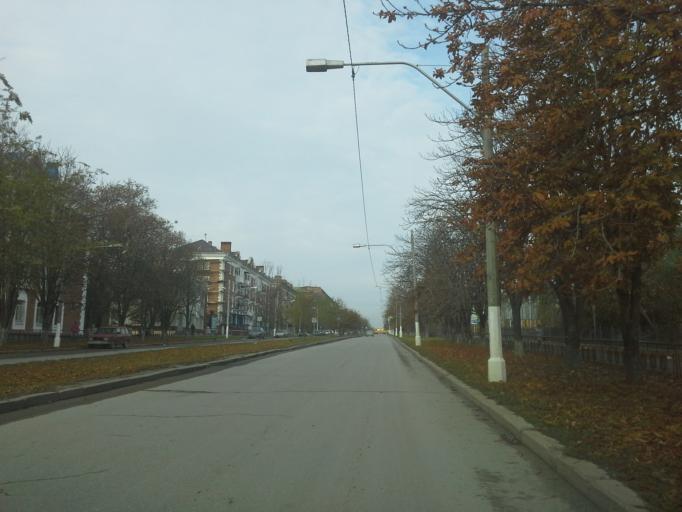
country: RU
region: Volgograd
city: Vodstroy
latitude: 48.7791
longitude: 44.5725
